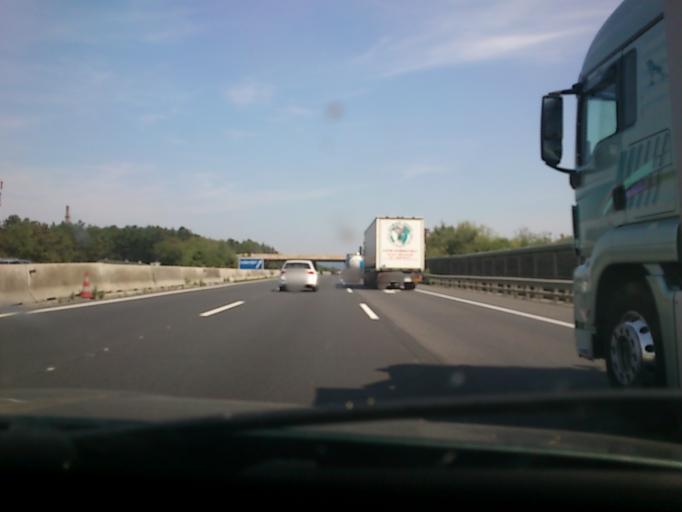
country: AT
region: Lower Austria
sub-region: Politischer Bezirk Baden
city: Leobersdorf
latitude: 47.9325
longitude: 16.2102
